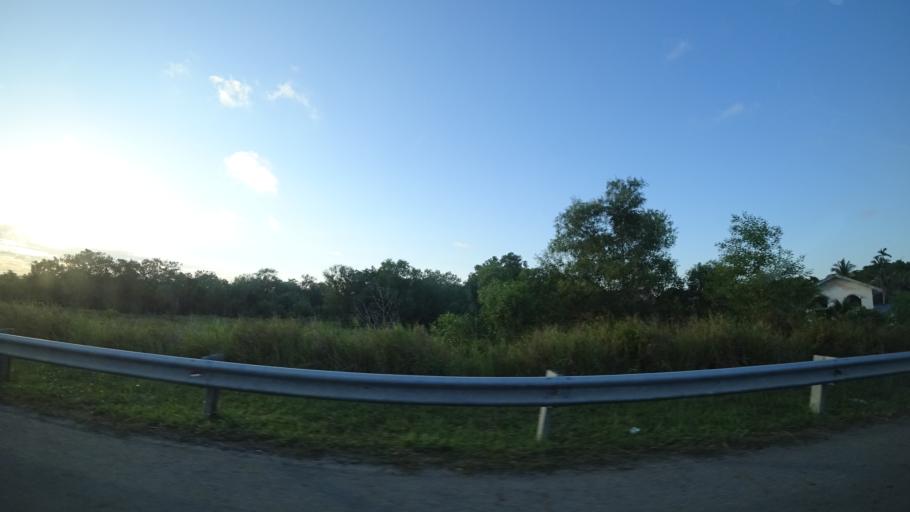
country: BN
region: Tutong
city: Tutong
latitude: 4.7986
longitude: 114.6477
